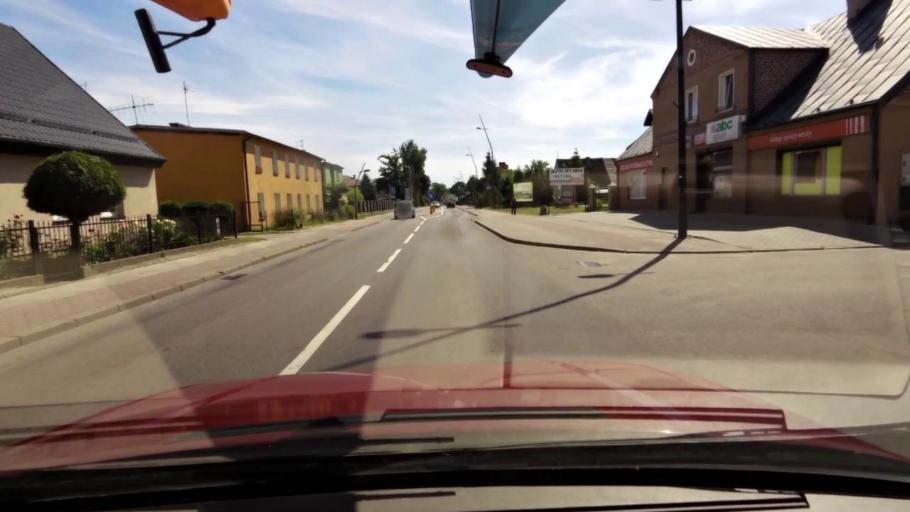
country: PL
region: Pomeranian Voivodeship
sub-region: Powiat slupski
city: Kobylnica
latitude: 54.4432
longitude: 16.9999
